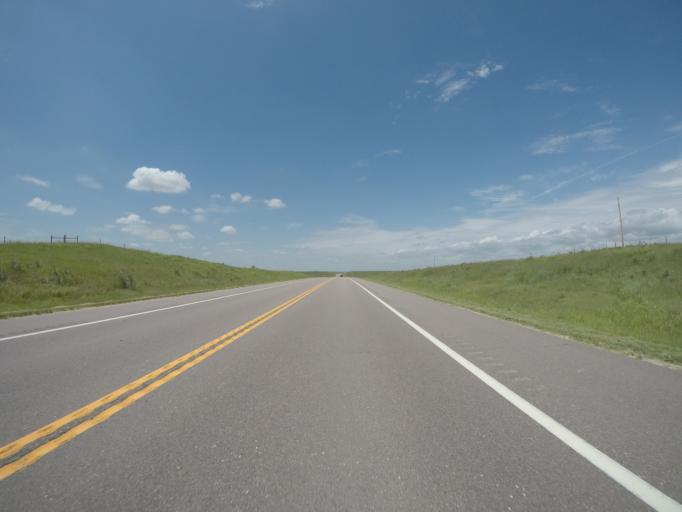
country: US
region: Kansas
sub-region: Graham County
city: Hill City
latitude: 39.3792
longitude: -99.7397
